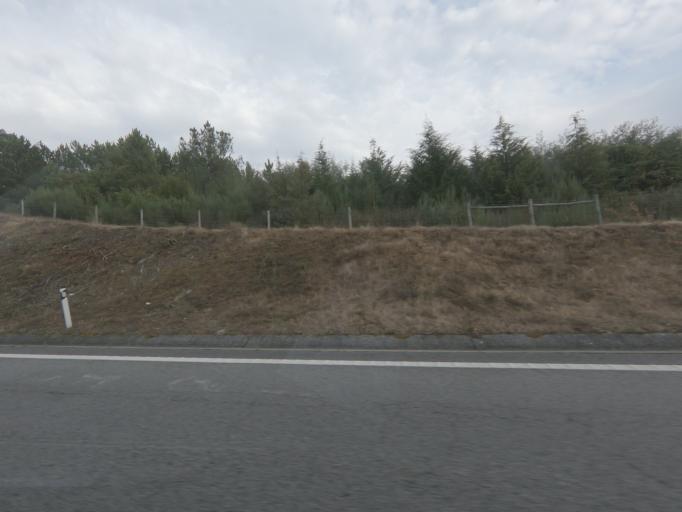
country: PT
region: Viseu
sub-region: Viseu
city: Campo
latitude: 40.7109
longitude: -7.9381
